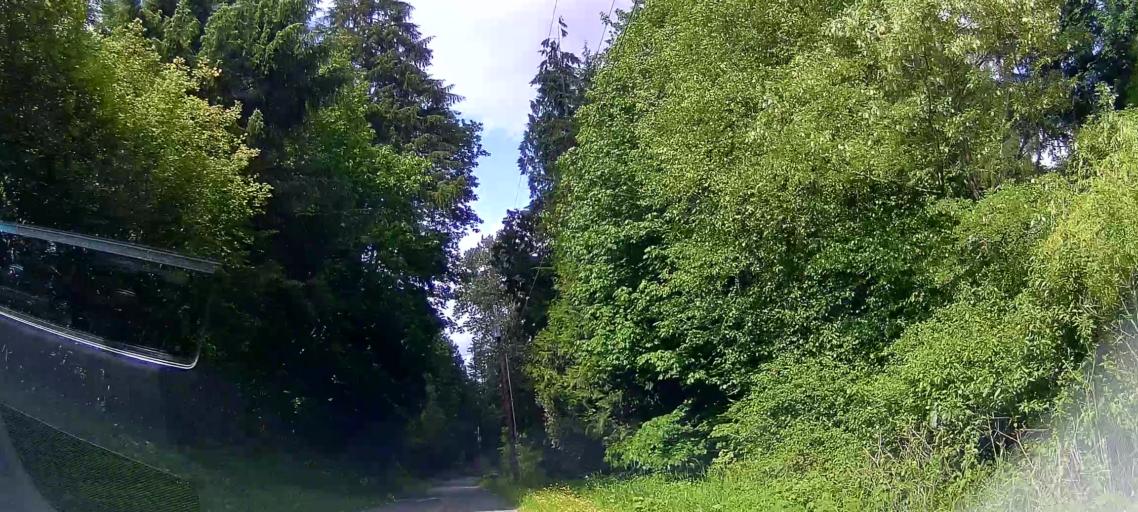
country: US
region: Washington
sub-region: Whatcom County
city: Sudden Valley
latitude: 48.6621
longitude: -122.1970
